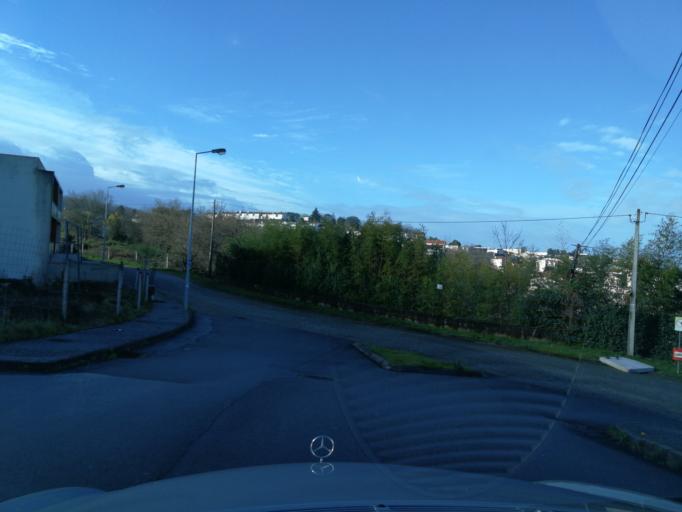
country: PT
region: Braga
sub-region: Braga
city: Braga
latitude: 41.5376
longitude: -8.3947
